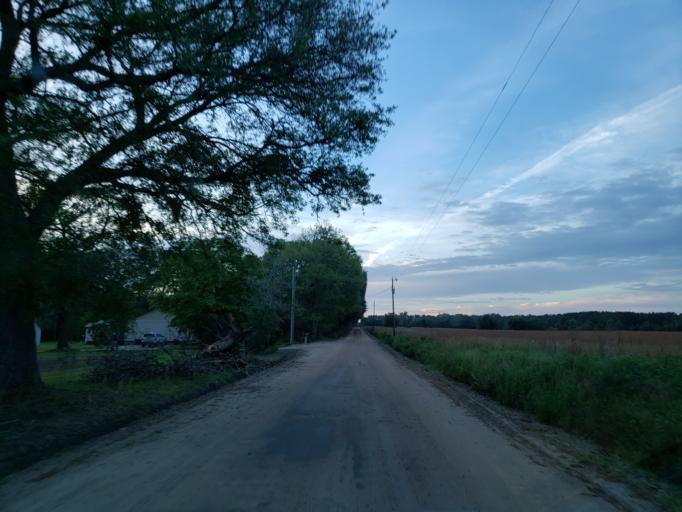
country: US
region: Georgia
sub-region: Lowndes County
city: Hahira
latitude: 30.9645
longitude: -83.3923
